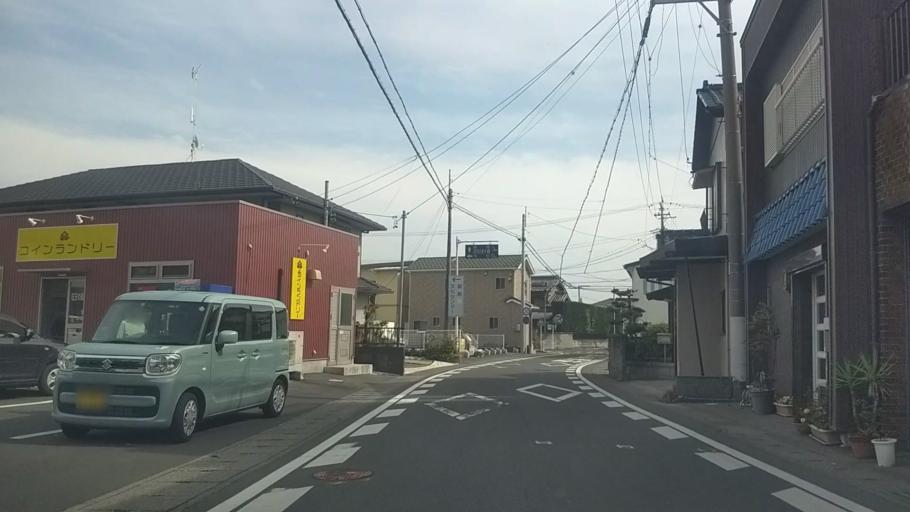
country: JP
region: Shizuoka
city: Kosai-shi
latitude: 34.7027
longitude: 137.6293
